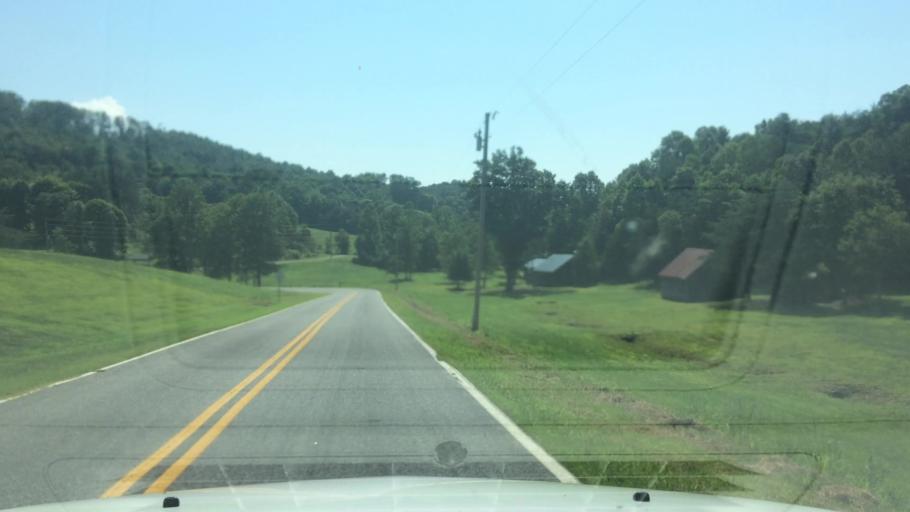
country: US
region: North Carolina
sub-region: Alexander County
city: Taylorsville
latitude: 35.9943
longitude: -81.2719
